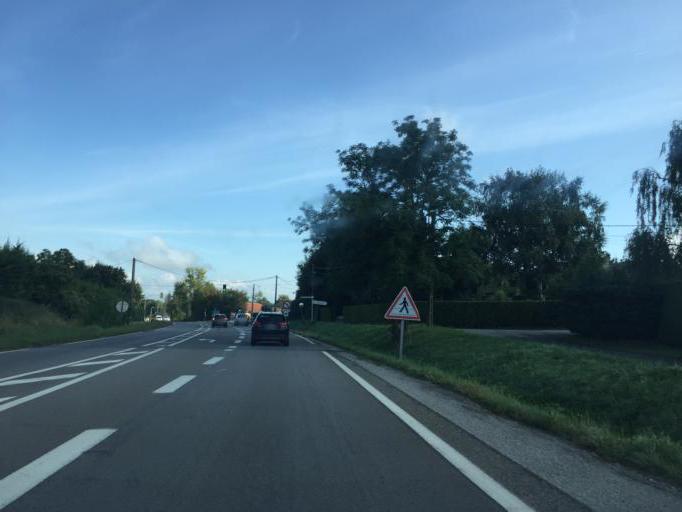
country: FR
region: Rhone-Alpes
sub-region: Departement de la Haute-Savoie
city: Beaumont
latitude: 46.0925
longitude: 6.1035
